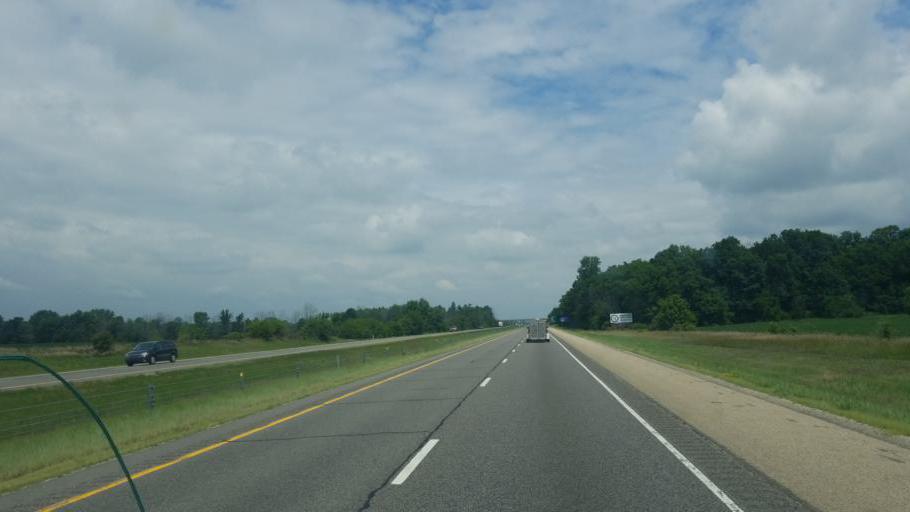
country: US
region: Indiana
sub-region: Delaware County
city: Yorktown
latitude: 40.2517
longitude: -85.5573
